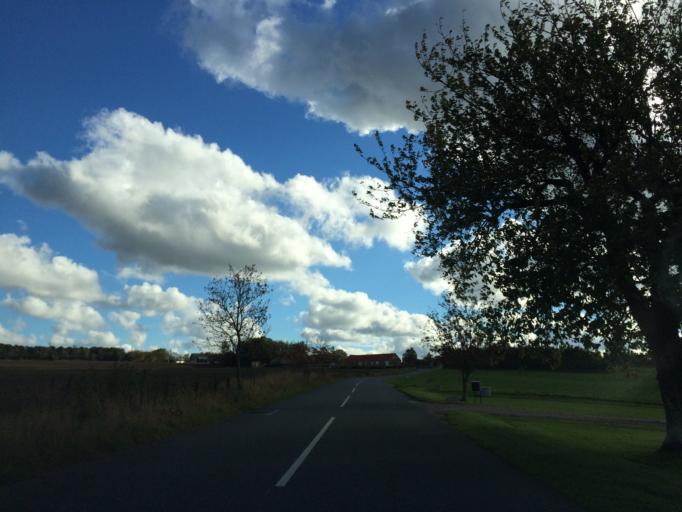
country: DK
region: Central Jutland
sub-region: Skanderborg Kommune
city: Ry
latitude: 56.1837
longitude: 9.7715
